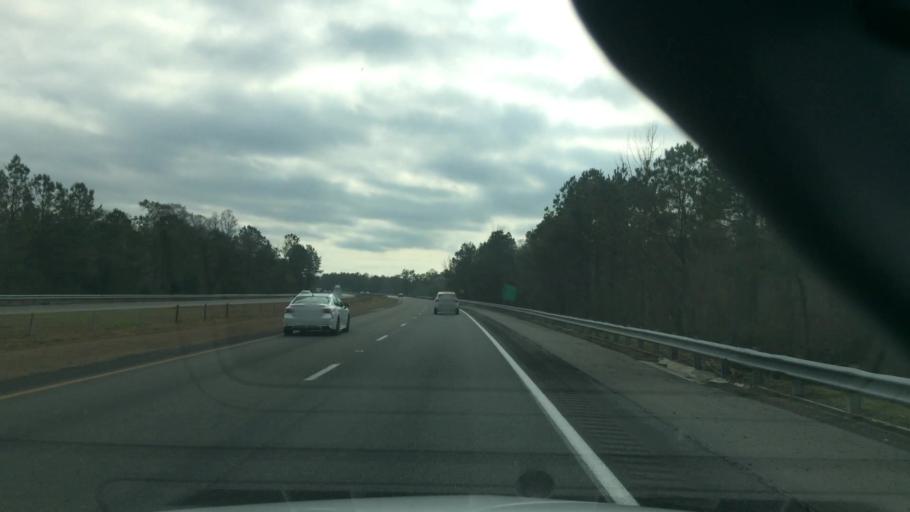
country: US
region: North Carolina
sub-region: New Hanover County
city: Castle Hayne
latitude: 34.3688
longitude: -77.8877
